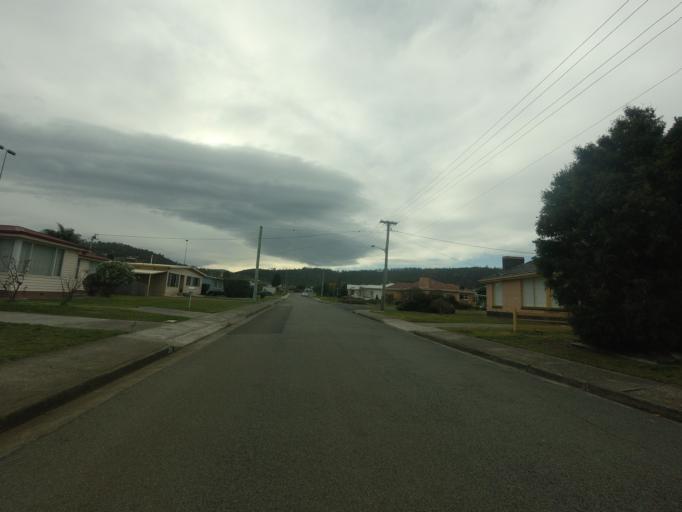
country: AU
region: Tasmania
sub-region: Clarence
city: Howrah
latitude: -42.8798
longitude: 147.3963
